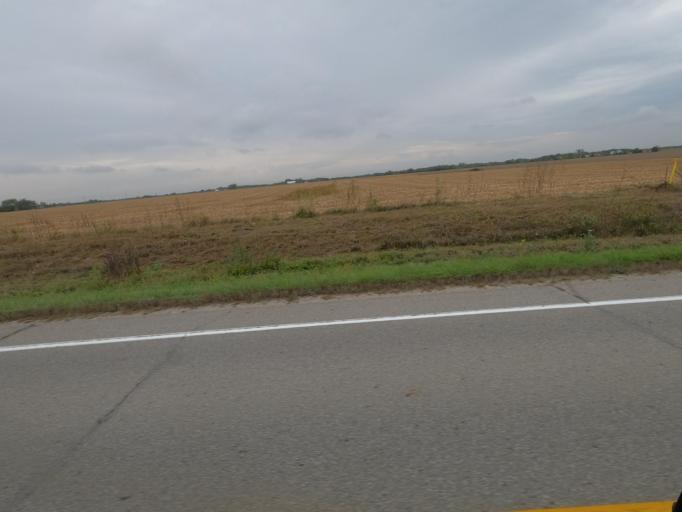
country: US
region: Iowa
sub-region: Van Buren County
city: Keosauqua
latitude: 40.8135
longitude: -91.8972
